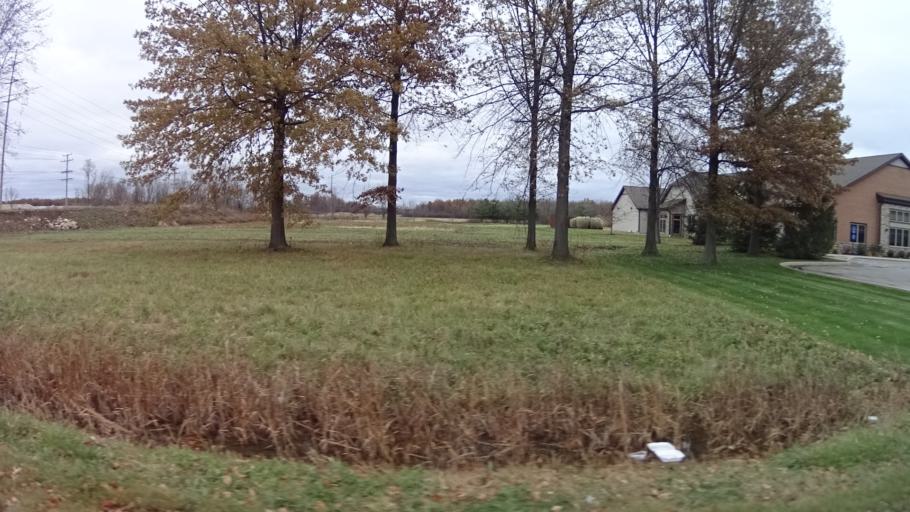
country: US
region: Ohio
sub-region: Lorain County
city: Avon
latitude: 41.4777
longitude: -82.0478
